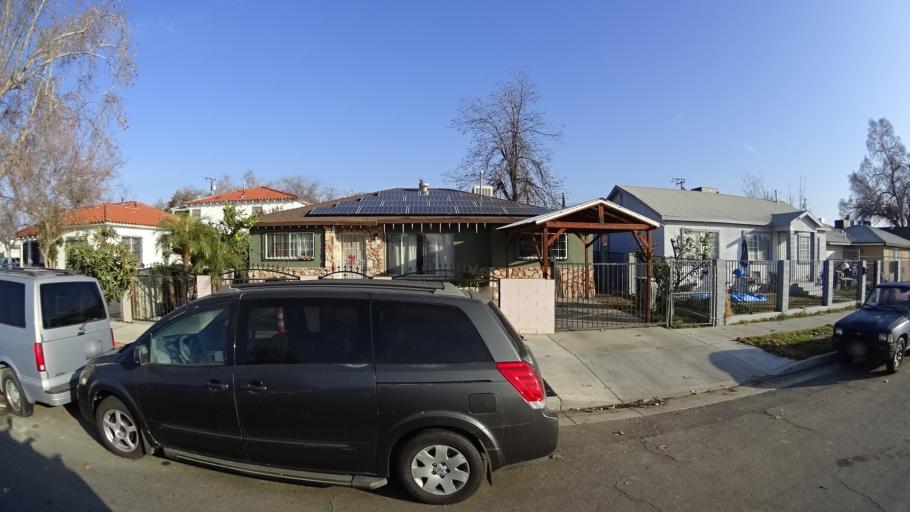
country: US
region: California
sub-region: Kern County
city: Bakersfield
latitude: 35.3807
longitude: -118.9809
